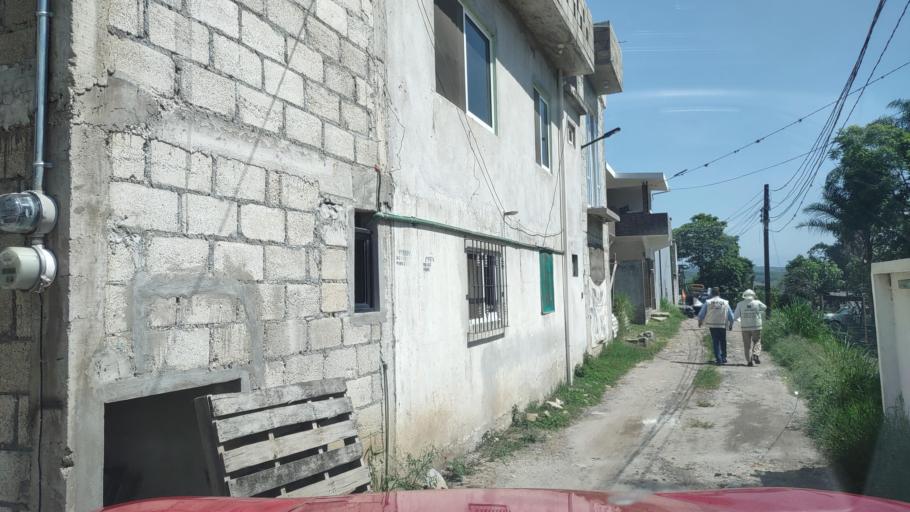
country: MX
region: Veracruz
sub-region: Emiliano Zapata
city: Dos Rios
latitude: 19.4902
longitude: -96.8151
